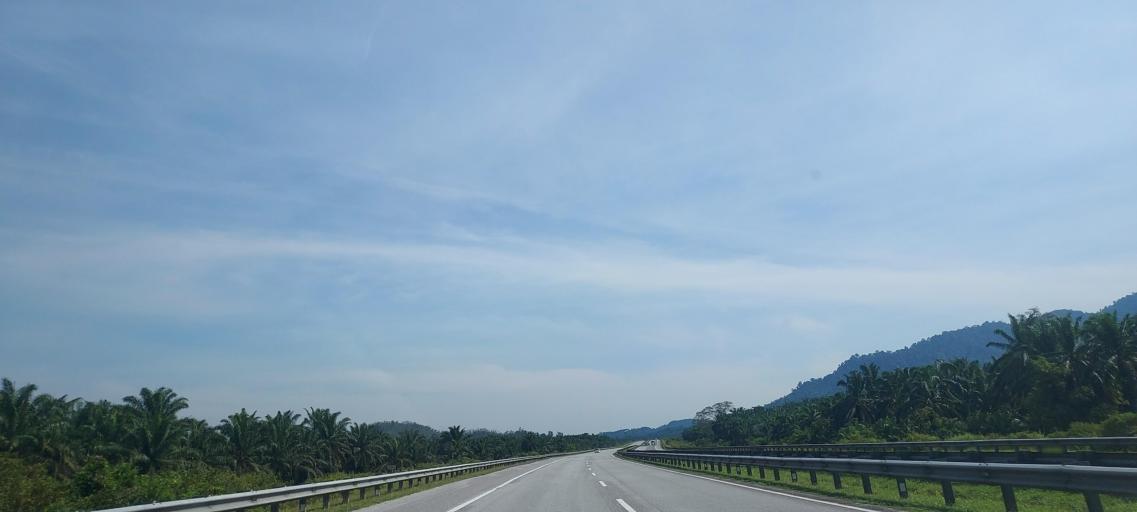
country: MY
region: Terengganu
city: Marang
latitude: 4.9653
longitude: 103.0812
